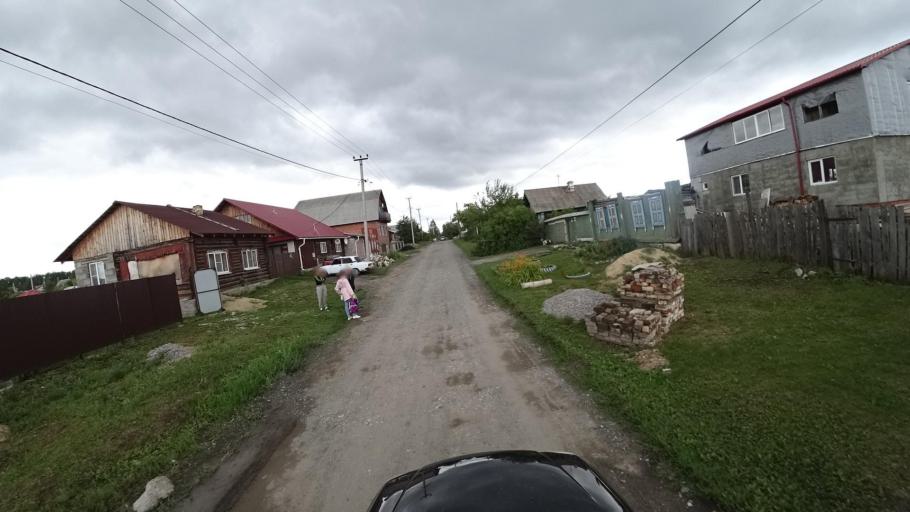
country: RU
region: Sverdlovsk
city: Kamyshlov
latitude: 56.8521
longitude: 62.6857
